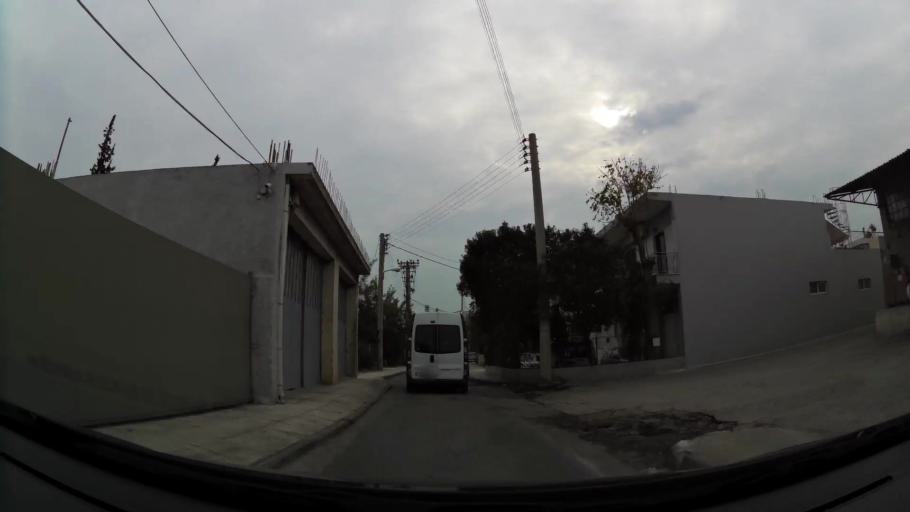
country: GR
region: Attica
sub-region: Nomarchia Athinas
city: Tavros
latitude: 37.9716
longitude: 23.6893
